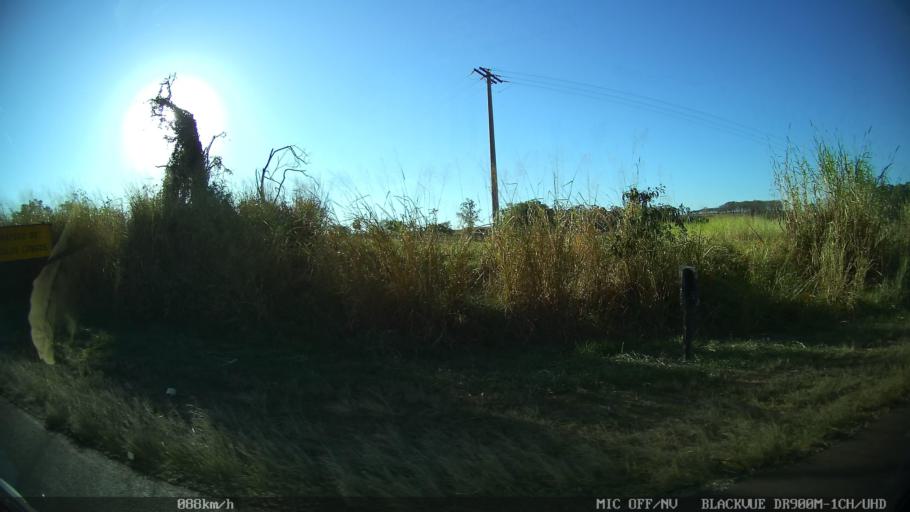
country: BR
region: Sao Paulo
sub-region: Guapiacu
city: Guapiacu
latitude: -20.7667
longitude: -49.2006
